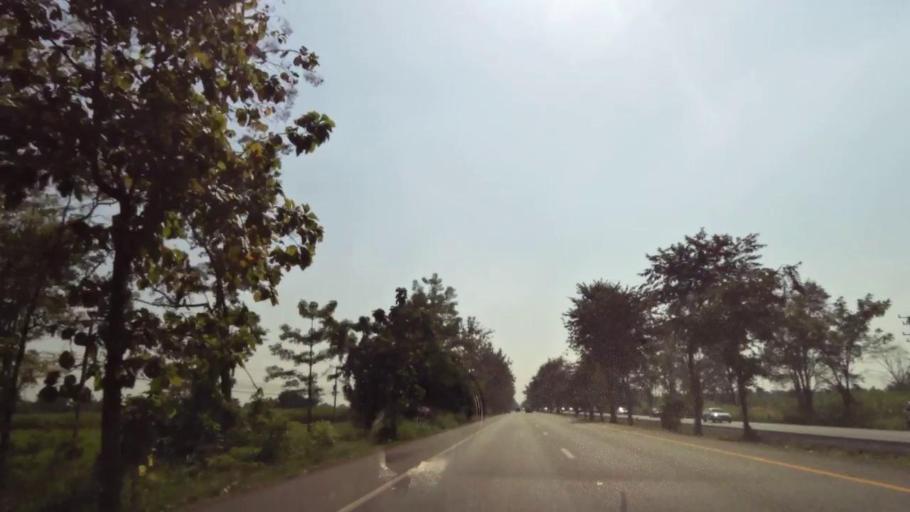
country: TH
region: Phichit
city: Bueng Na Rang
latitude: 16.0826
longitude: 100.1246
